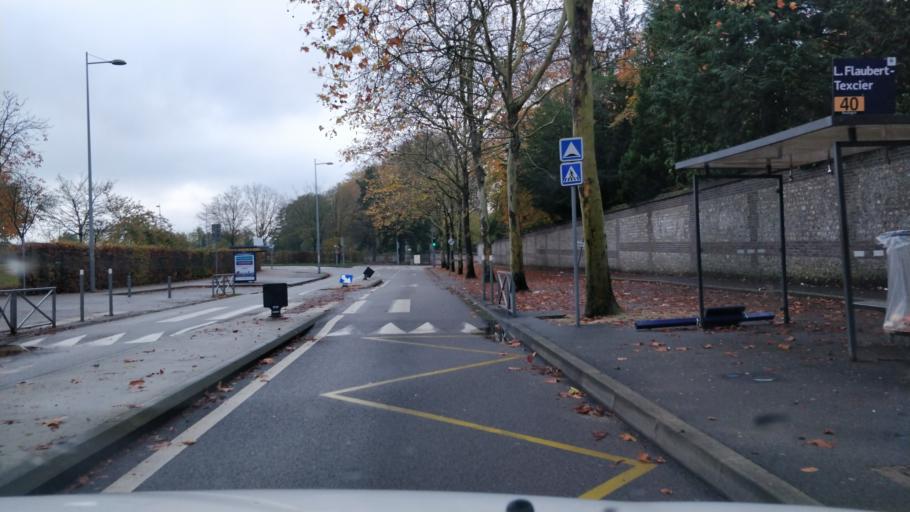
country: FR
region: Haute-Normandie
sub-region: Departement de la Seine-Maritime
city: Bihorel
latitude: 49.4509
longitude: 1.1202
